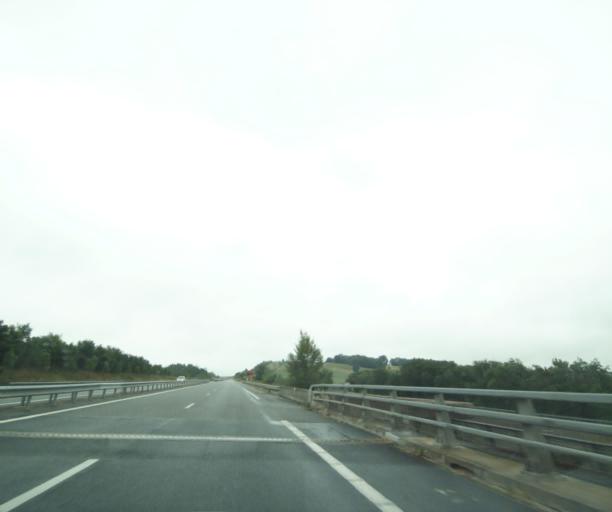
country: FR
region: Midi-Pyrenees
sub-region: Departement du Tarn
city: Carmaux
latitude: 44.0418
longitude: 2.2080
